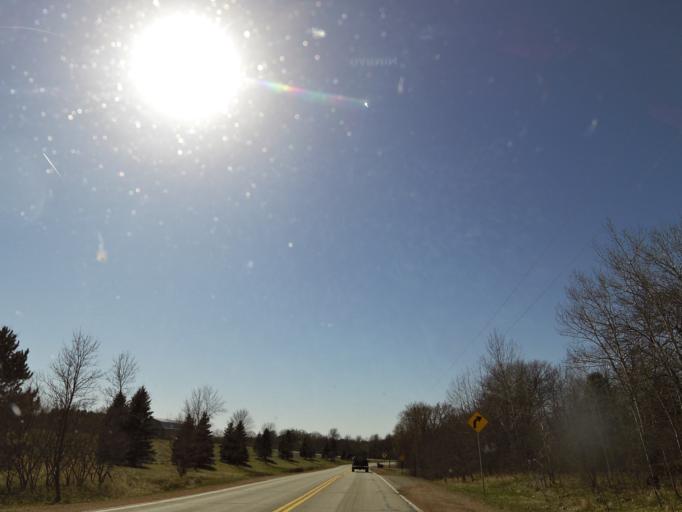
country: US
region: Minnesota
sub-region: Scott County
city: Prior Lake
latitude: 44.6686
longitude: -93.3620
